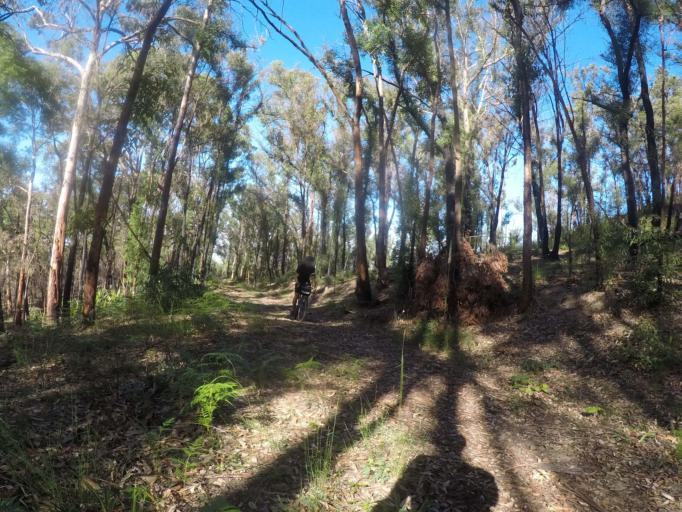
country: AU
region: New South Wales
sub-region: Hornsby Shire
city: Glenorie
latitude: -33.3428
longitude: 151.0493
